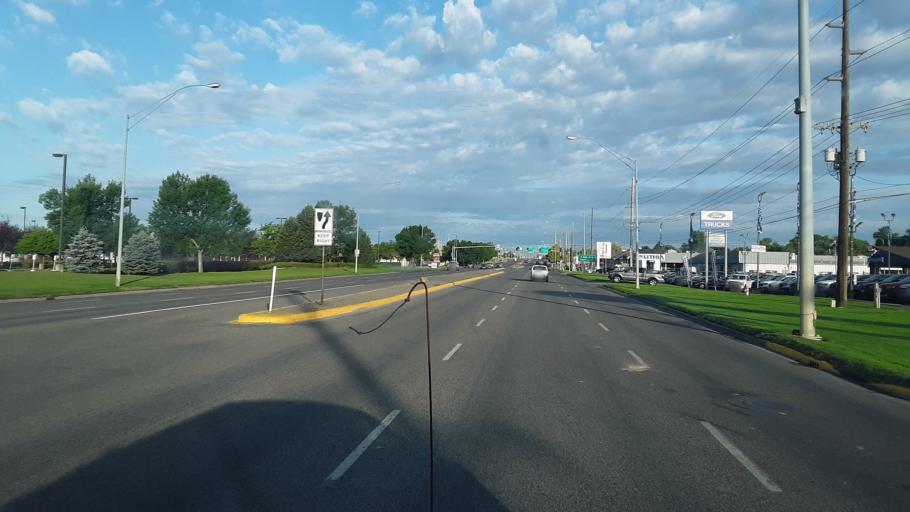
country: US
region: Montana
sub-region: Yellowstone County
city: Billings
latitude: 45.7552
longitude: -108.5698
